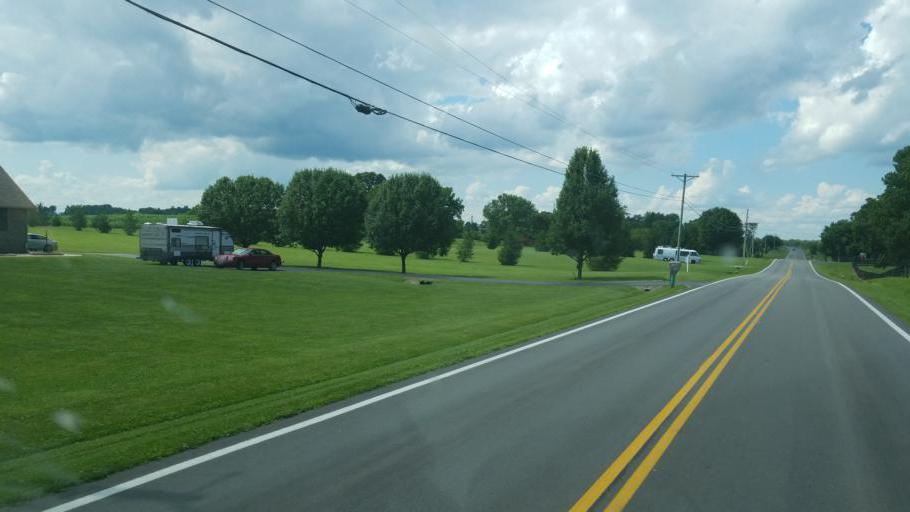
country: US
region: Ohio
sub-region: Highland County
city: Greenfield
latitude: 39.3697
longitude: -83.3787
